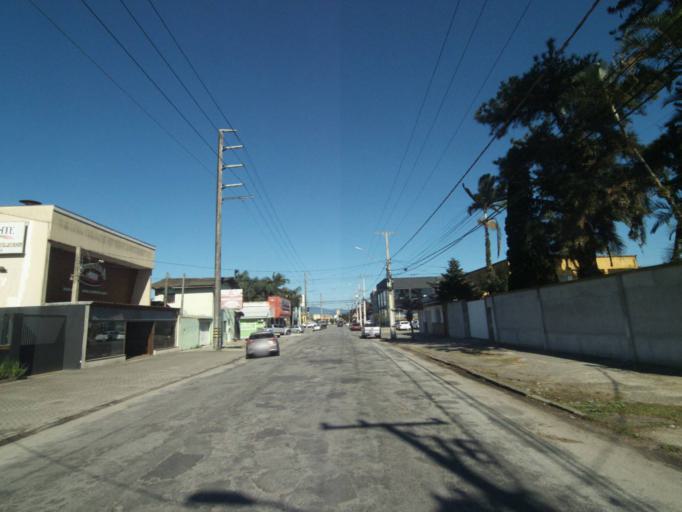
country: BR
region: Parana
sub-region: Paranagua
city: Paranagua
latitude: -25.5223
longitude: -48.5205
